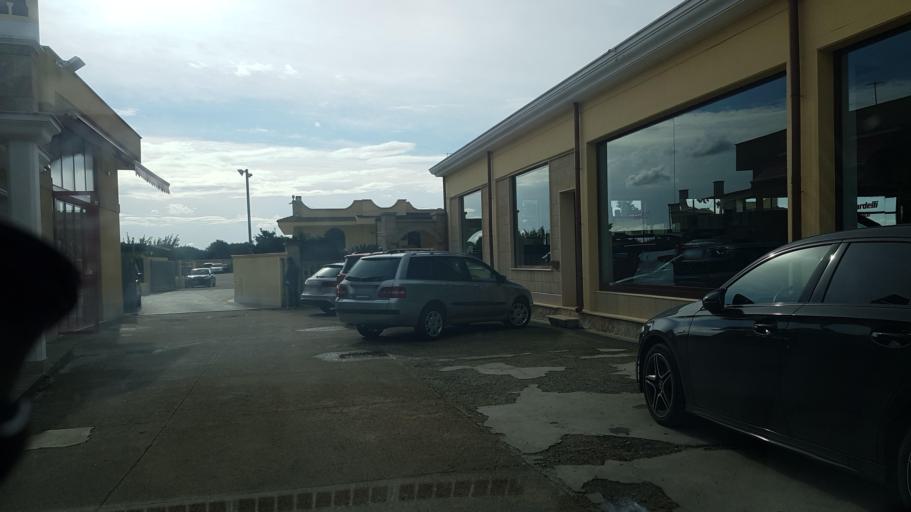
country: IT
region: Apulia
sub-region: Provincia di Brindisi
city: San Vito dei Normanni
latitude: 40.6566
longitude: 17.7294
